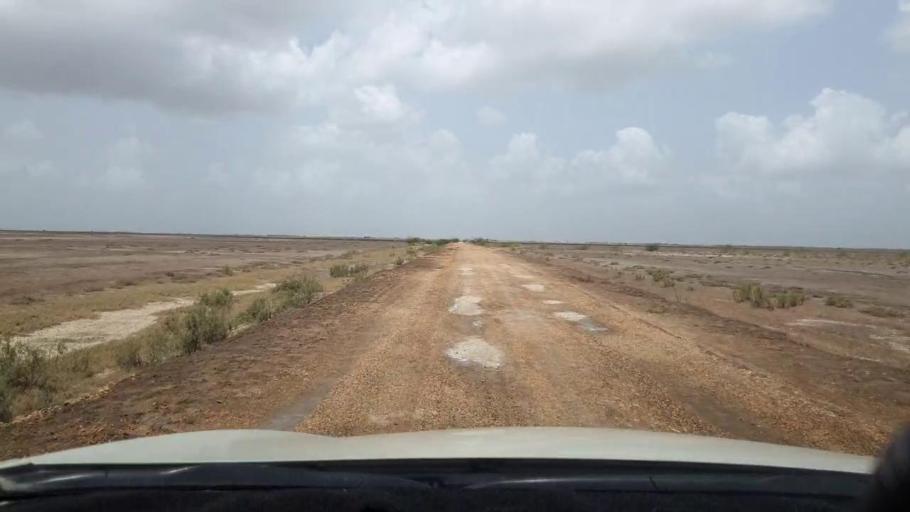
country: PK
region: Sindh
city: Kadhan
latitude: 24.3603
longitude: 68.8390
